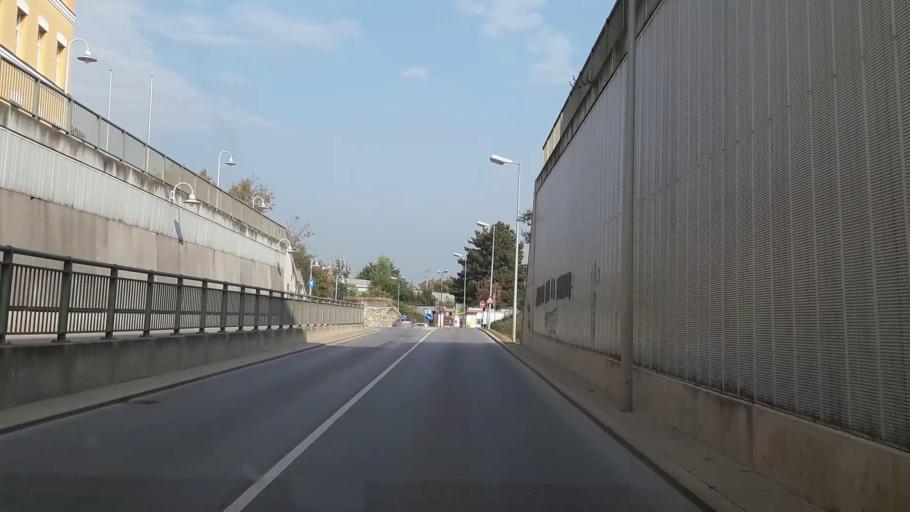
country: AT
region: Lower Austria
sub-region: Politischer Bezirk Wien-Umgebung
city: Schwechat
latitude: 48.1486
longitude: 16.4710
